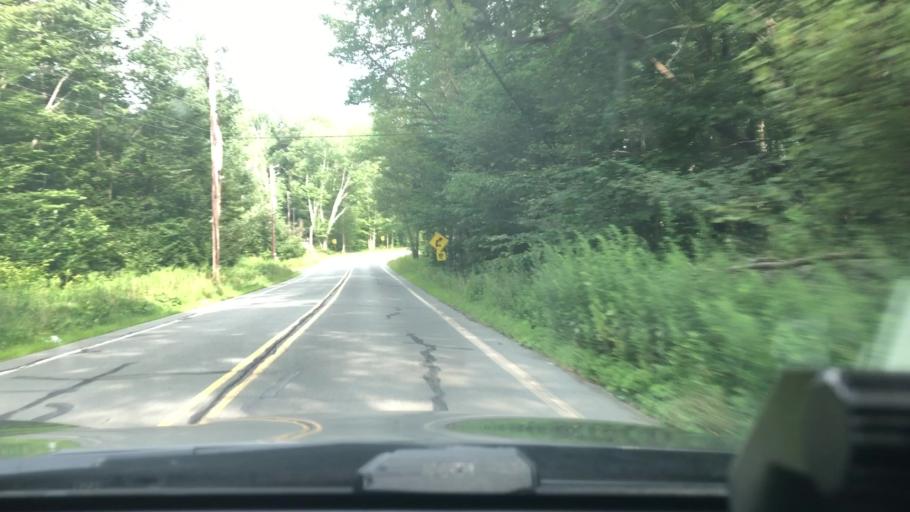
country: US
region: Pennsylvania
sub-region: Lackawanna County
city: Moscow
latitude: 41.2489
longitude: -75.4918
